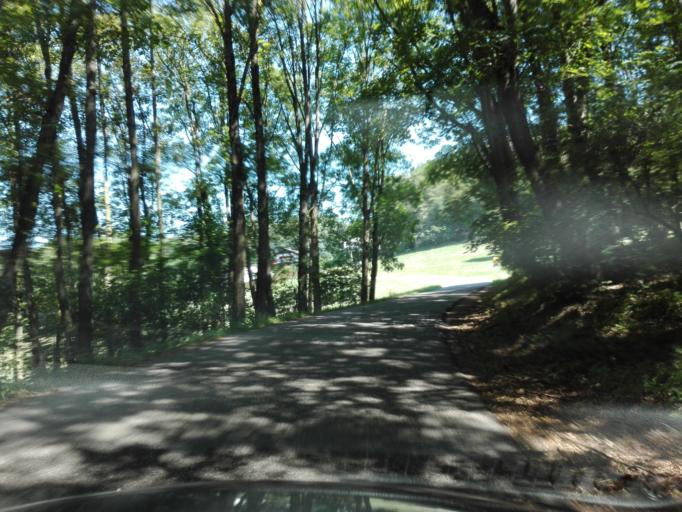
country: AT
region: Upper Austria
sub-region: Politischer Bezirk Urfahr-Umgebung
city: Steyregg
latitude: 48.2941
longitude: 14.3723
